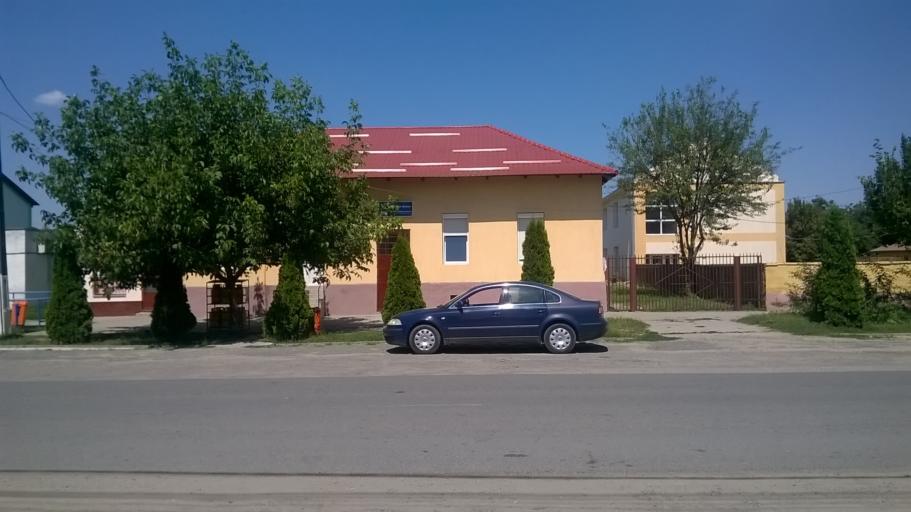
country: RO
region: Timis
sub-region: Comuna Dudestii Vechi
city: Dudestii Vechi
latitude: 46.0425
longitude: 20.4750
